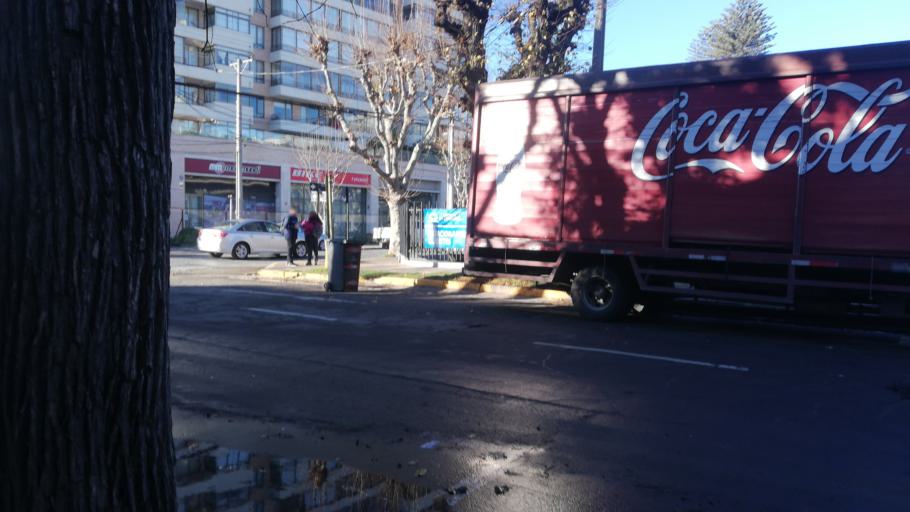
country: CL
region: Valparaiso
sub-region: Provincia de Valparaiso
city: Vina del Mar
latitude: -33.0189
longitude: -71.5469
